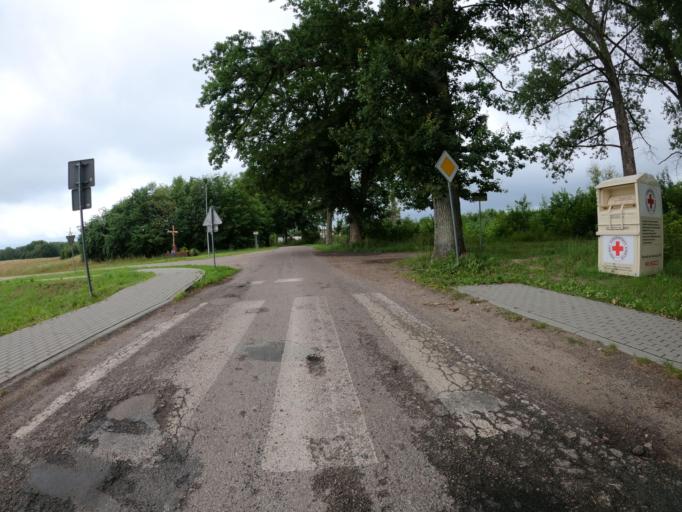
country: PL
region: West Pomeranian Voivodeship
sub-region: Powiat szczecinecki
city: Grzmiaca
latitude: 53.9349
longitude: 16.4528
